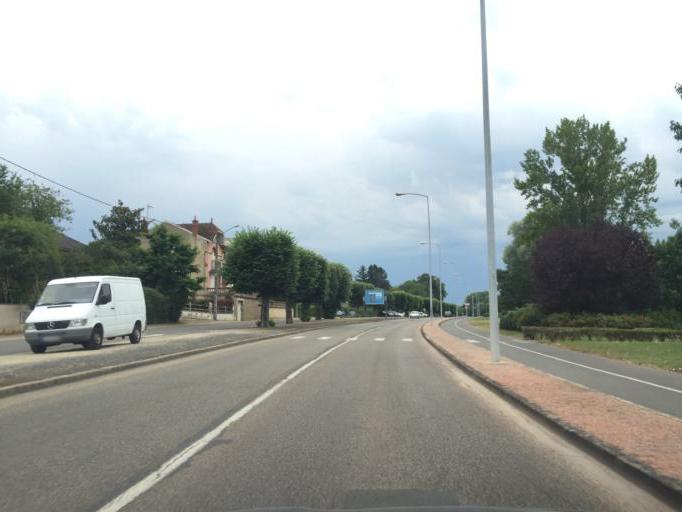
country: FR
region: Auvergne
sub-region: Departement de l'Allier
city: Moulins
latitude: 46.5538
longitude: 3.3309
